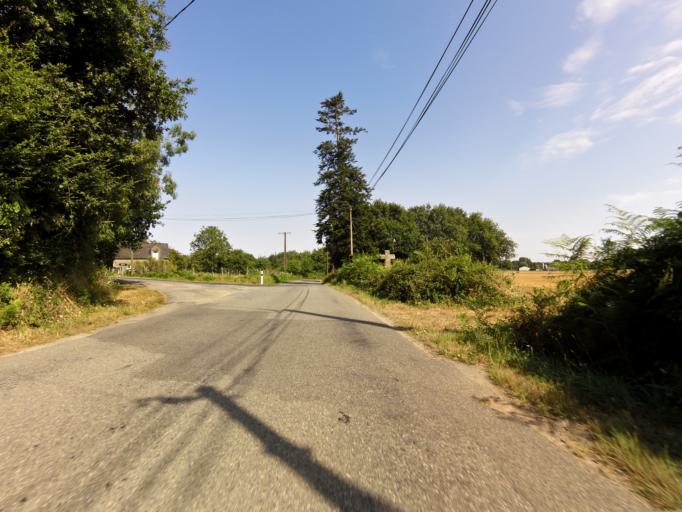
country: FR
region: Brittany
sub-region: Departement du Morbihan
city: Limerzel
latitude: 47.6574
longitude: -2.3996
